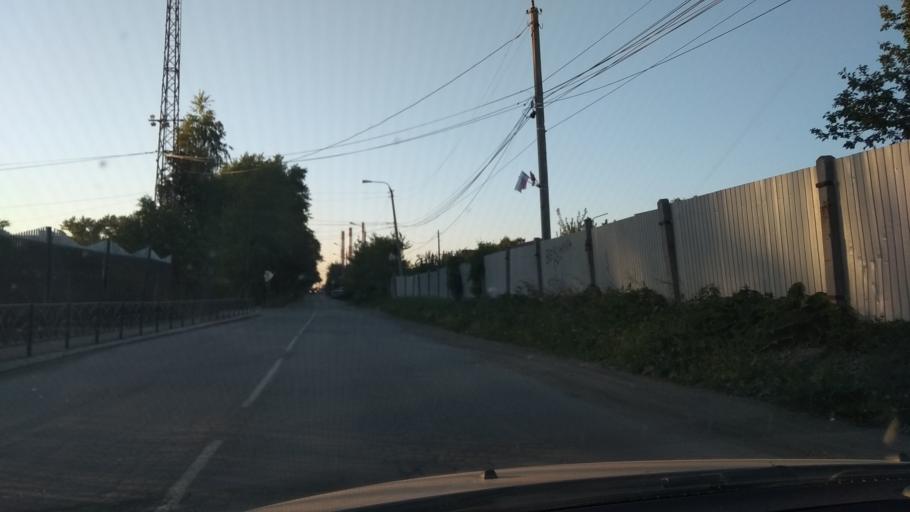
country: RU
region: Sverdlovsk
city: Sredneuralsk
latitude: 56.9847
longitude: 60.4599
